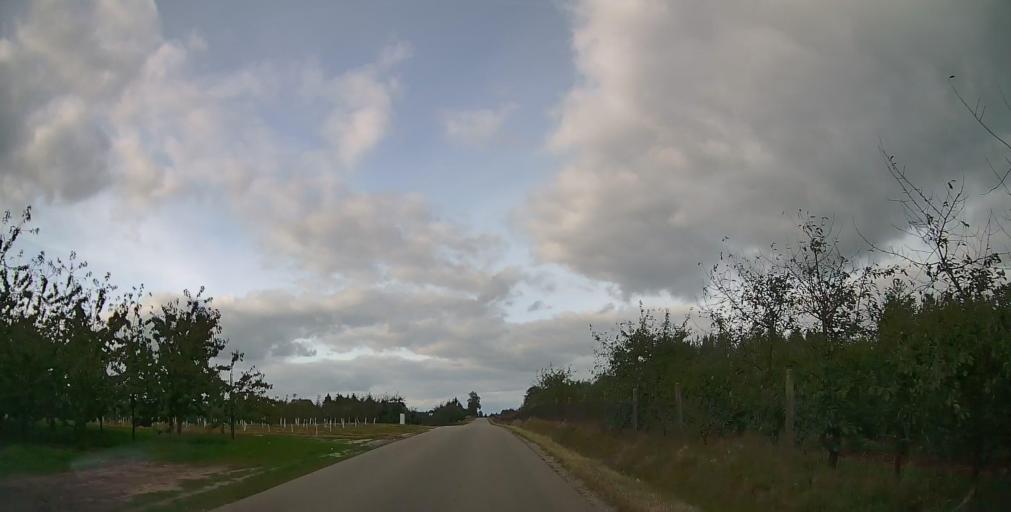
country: PL
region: Masovian Voivodeship
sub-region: Powiat bialobrzeski
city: Promna
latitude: 51.7144
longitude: 20.9583
